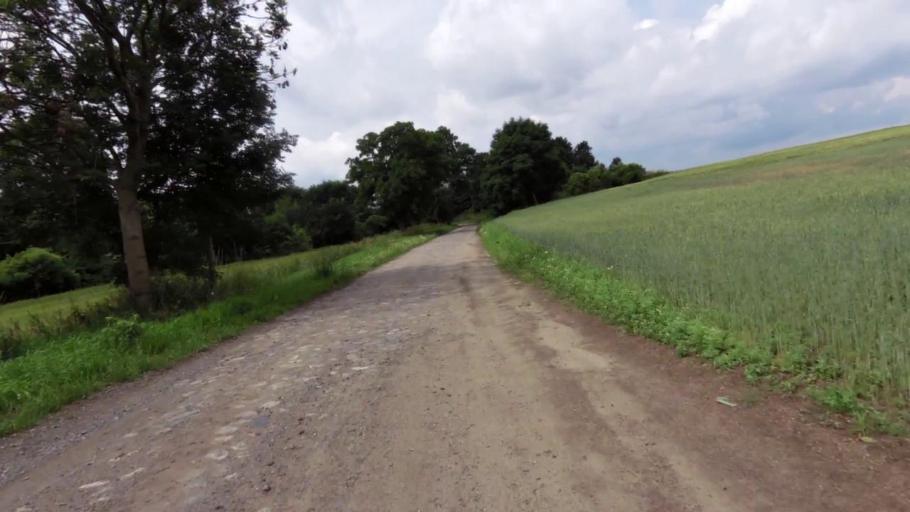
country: PL
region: West Pomeranian Voivodeship
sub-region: Powiat mysliborski
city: Mysliborz
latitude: 52.9764
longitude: 14.8913
